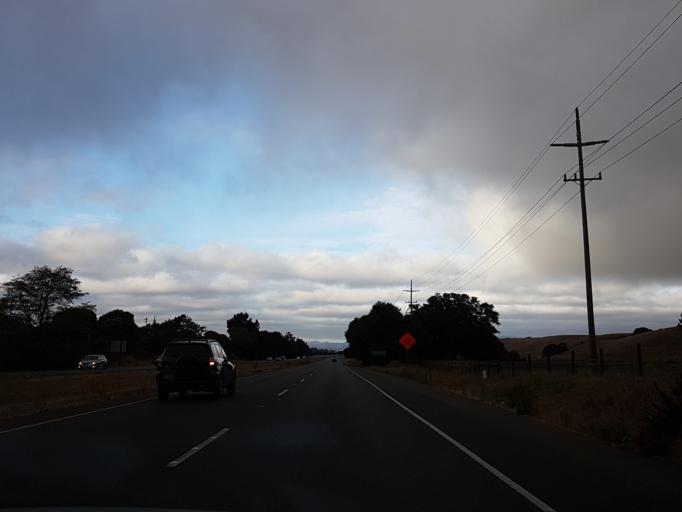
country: US
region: California
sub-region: Monterey County
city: Salinas
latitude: 36.6136
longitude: -121.6892
